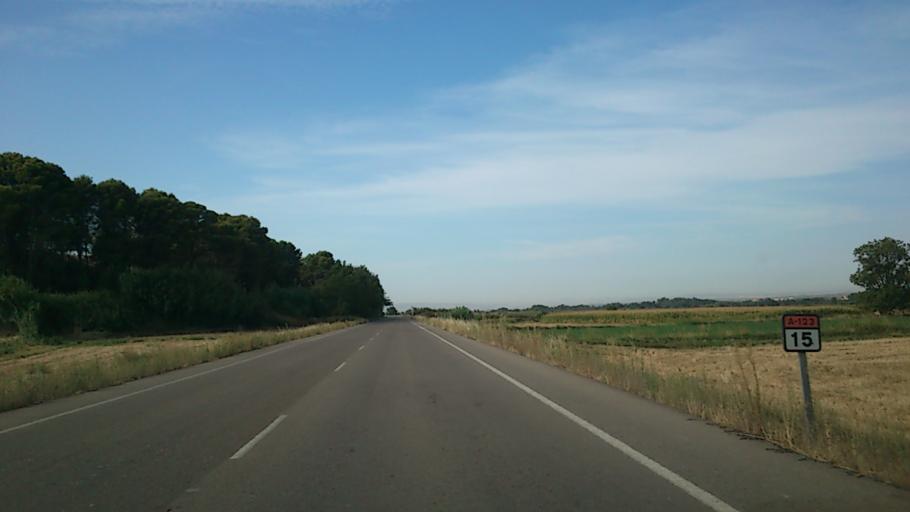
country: ES
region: Aragon
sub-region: Provincia de Zaragoza
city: Villanueva de Gallego
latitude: 41.7891
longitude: -0.7843
